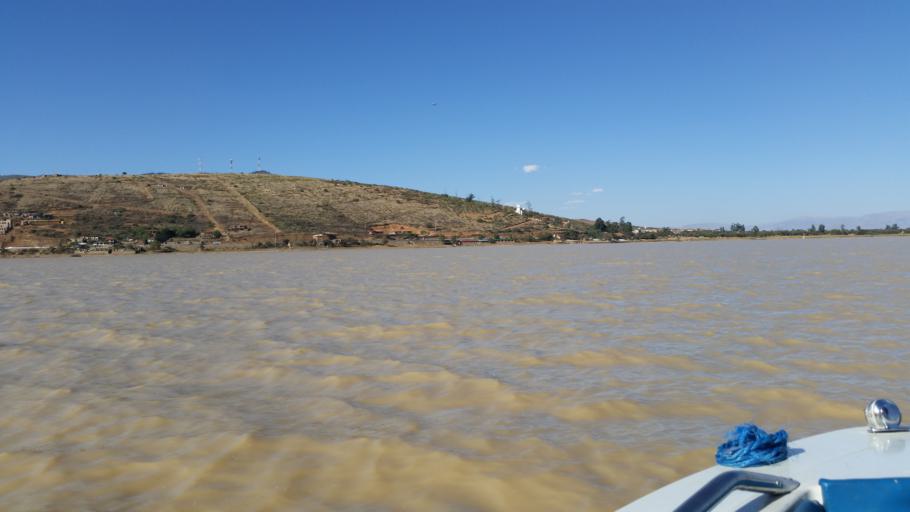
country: BO
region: Cochabamba
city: Tarata
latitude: -17.5354
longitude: -66.0906
